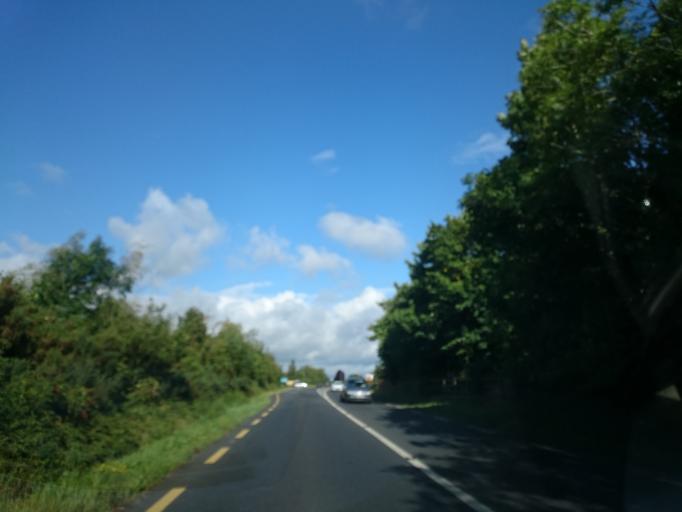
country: IE
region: Leinster
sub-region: Kilkenny
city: Kilkenny
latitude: 52.6950
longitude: -7.2616
